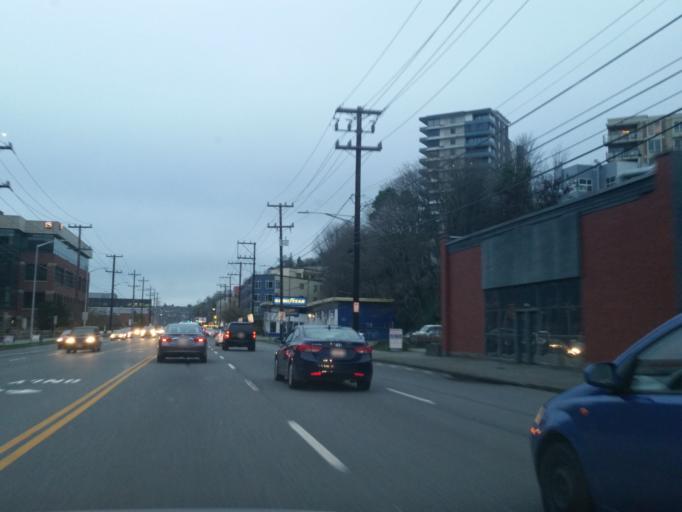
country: US
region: Washington
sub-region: King County
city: Seattle
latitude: 47.6223
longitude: -122.3628
